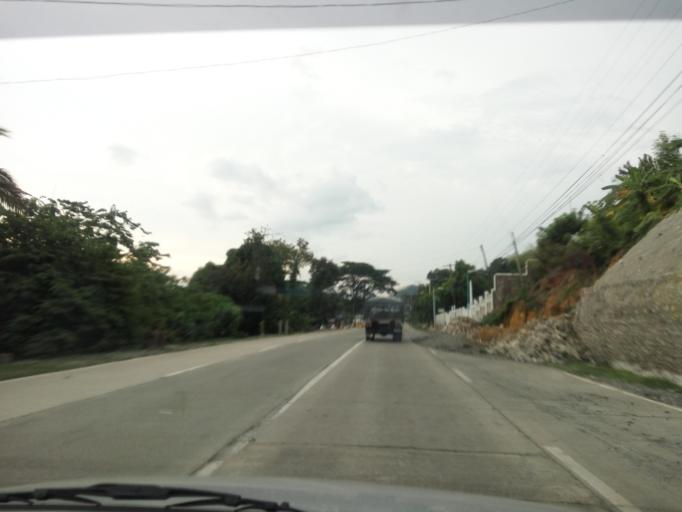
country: PH
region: Ilocos
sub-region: Province of Pangasinan
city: Sagunto
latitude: 16.1996
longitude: 120.5149
